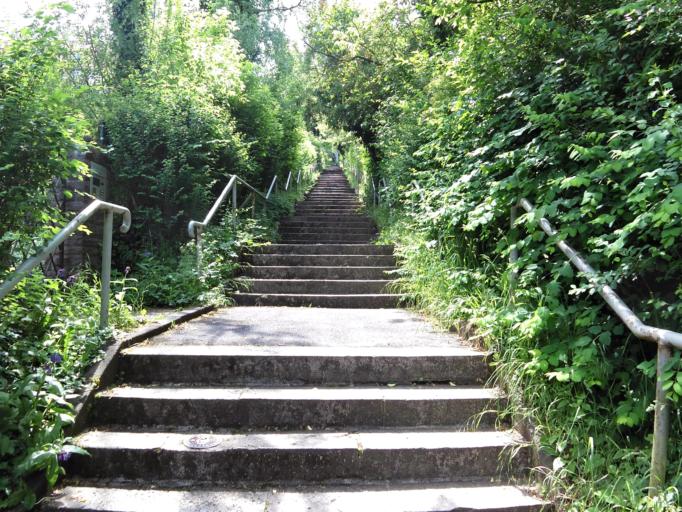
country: DE
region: Bavaria
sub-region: Regierungsbezirk Unterfranken
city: Hochberg
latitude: 49.7922
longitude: 9.9061
